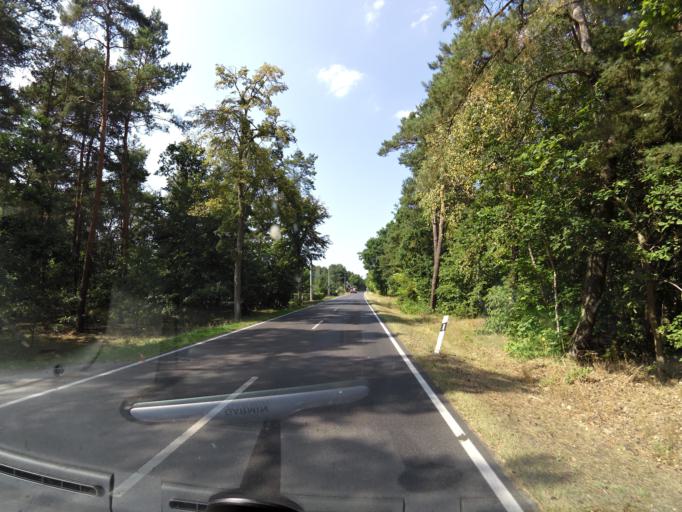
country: DE
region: Brandenburg
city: Zehdenick
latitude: 52.9659
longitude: 13.3641
